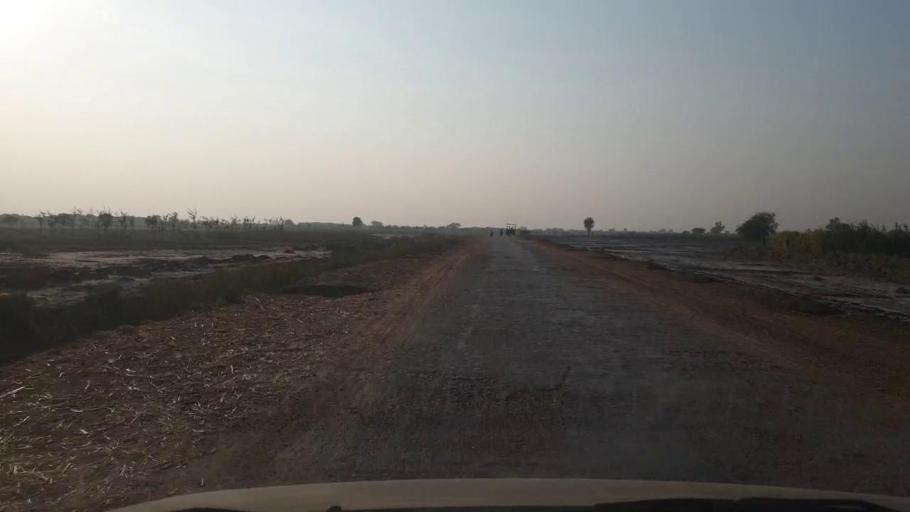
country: PK
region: Sindh
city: Mirwah Gorchani
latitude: 25.3682
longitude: 69.1350
